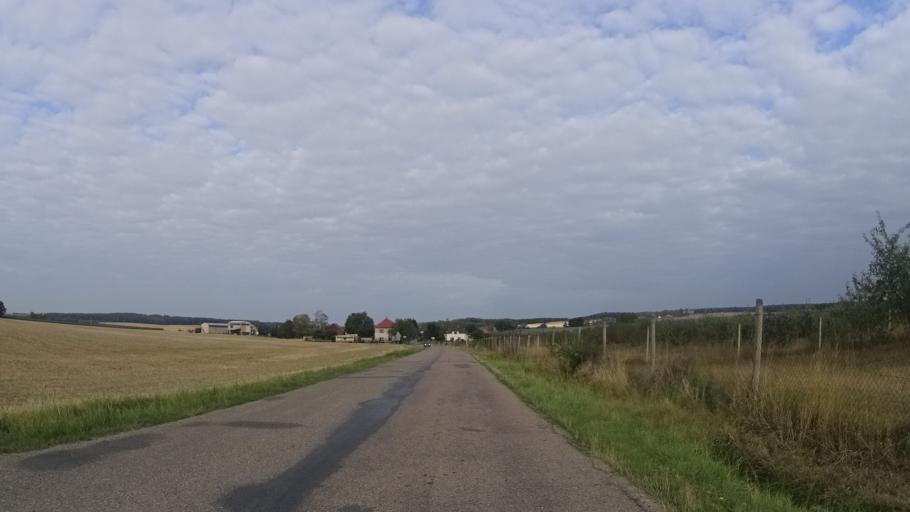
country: CZ
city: Stezery
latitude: 50.2086
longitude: 15.7024
